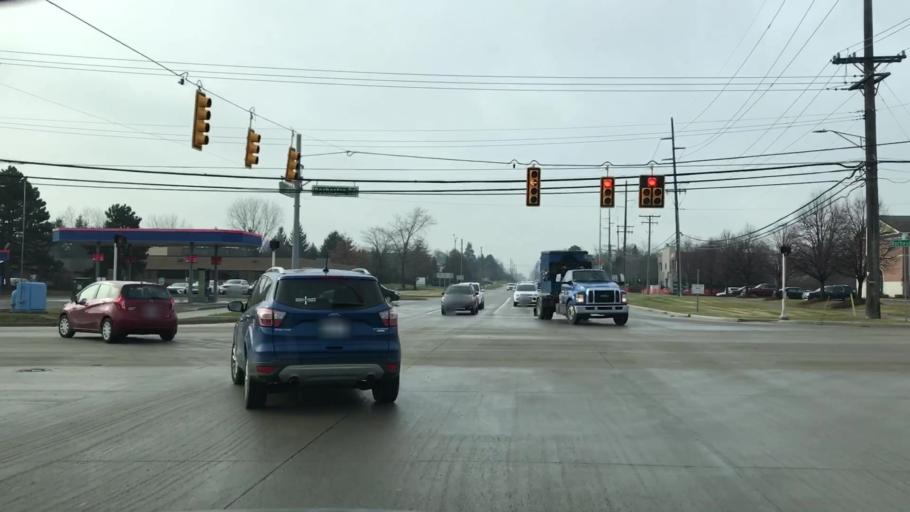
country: US
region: Michigan
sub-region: Oakland County
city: Troy
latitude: 42.6230
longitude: -83.1304
